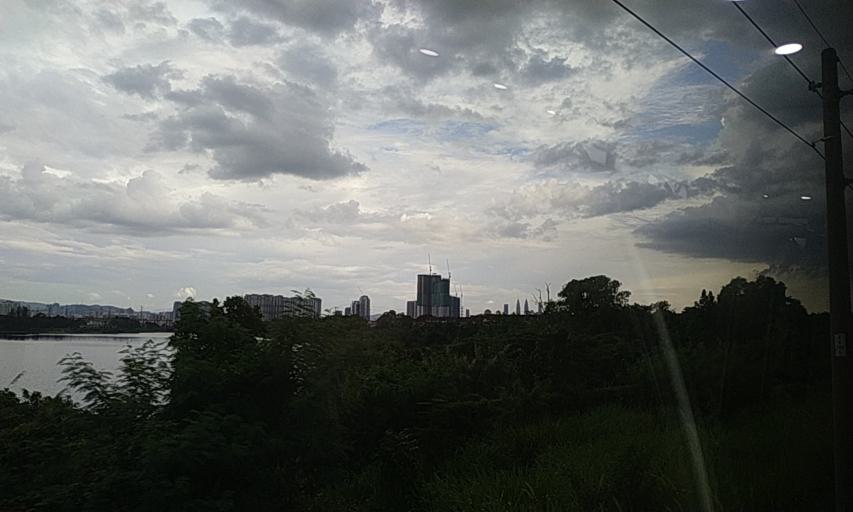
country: MY
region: Kuala Lumpur
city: Kuala Lumpur
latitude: 3.2219
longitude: 101.6726
